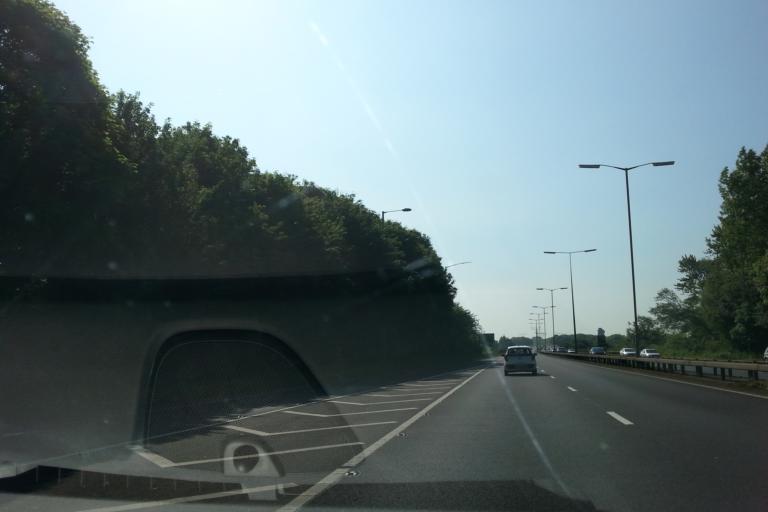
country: GB
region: England
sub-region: Peterborough
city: Peterborough
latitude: 52.5630
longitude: -0.2824
